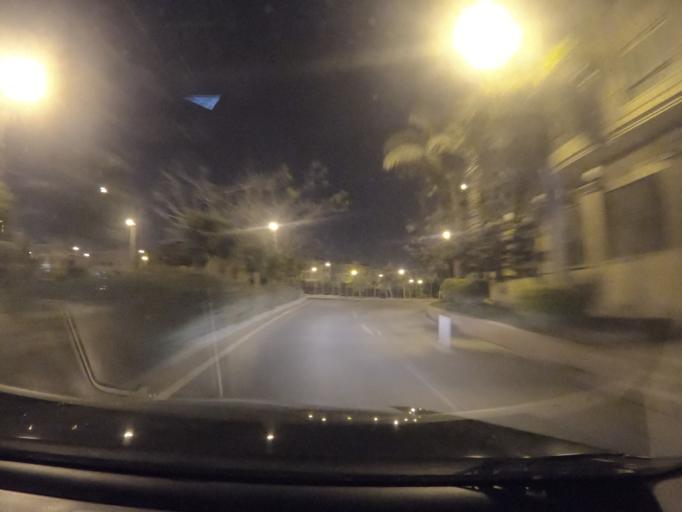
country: EG
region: Muhafazat al Qahirah
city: Cairo
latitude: 30.0156
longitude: 31.4193
